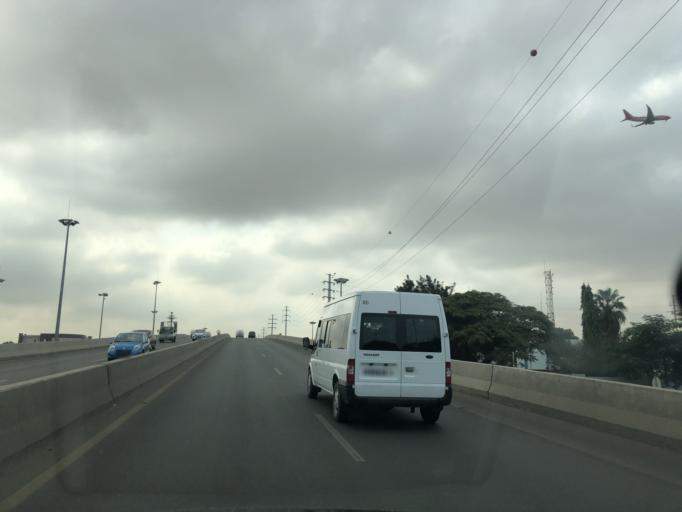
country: AO
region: Luanda
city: Luanda
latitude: -8.8337
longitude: 13.2544
